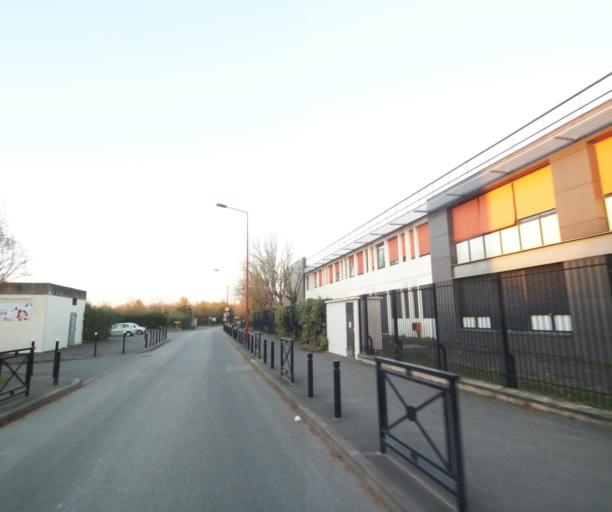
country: FR
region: Ile-de-France
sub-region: Departement du Val-d'Oise
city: Gonesse
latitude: 48.9884
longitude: 2.4400
